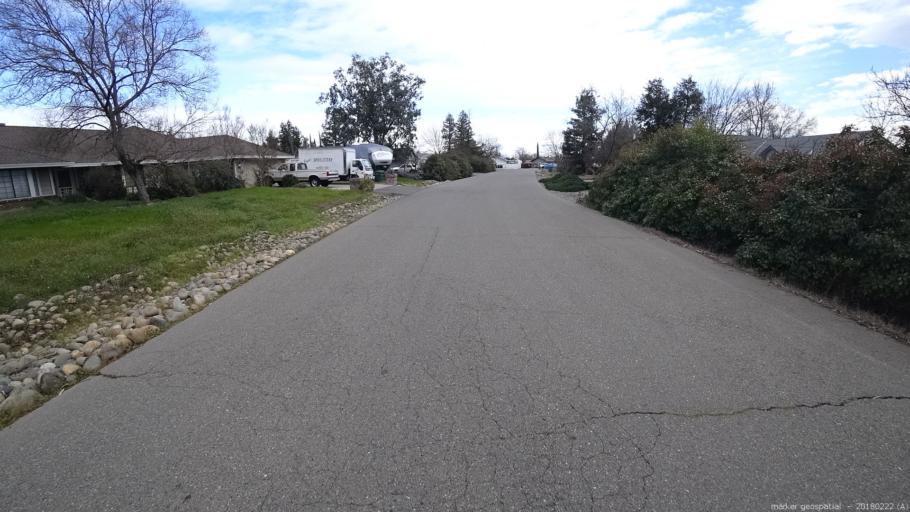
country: US
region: California
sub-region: Sacramento County
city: Rio Linda
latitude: 38.7125
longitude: -121.4161
